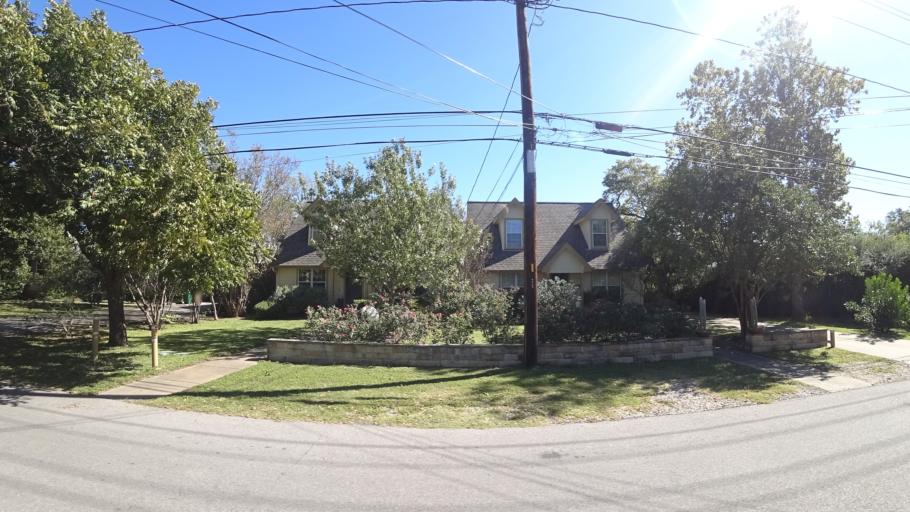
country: US
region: Texas
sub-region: Travis County
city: Austin
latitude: 30.3306
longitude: -97.7415
